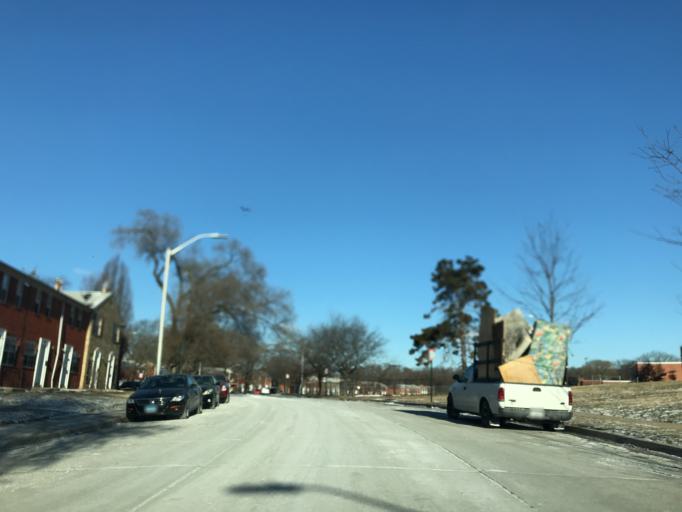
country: US
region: Maryland
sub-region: City of Baltimore
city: Baltimore
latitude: 39.2988
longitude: -76.6597
